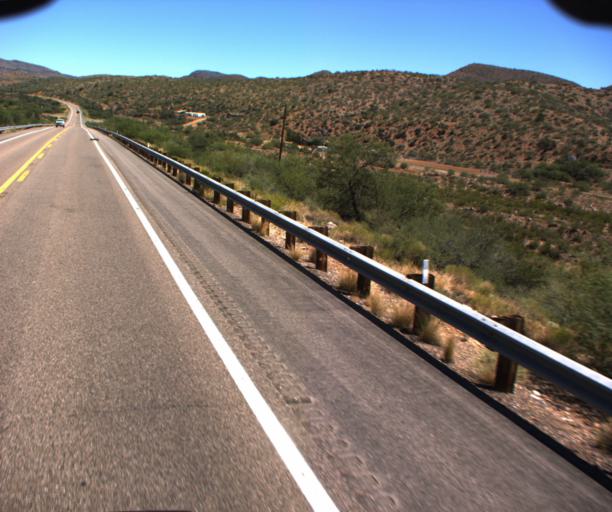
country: US
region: Arizona
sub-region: Gila County
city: Globe
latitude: 33.4432
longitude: -110.7224
